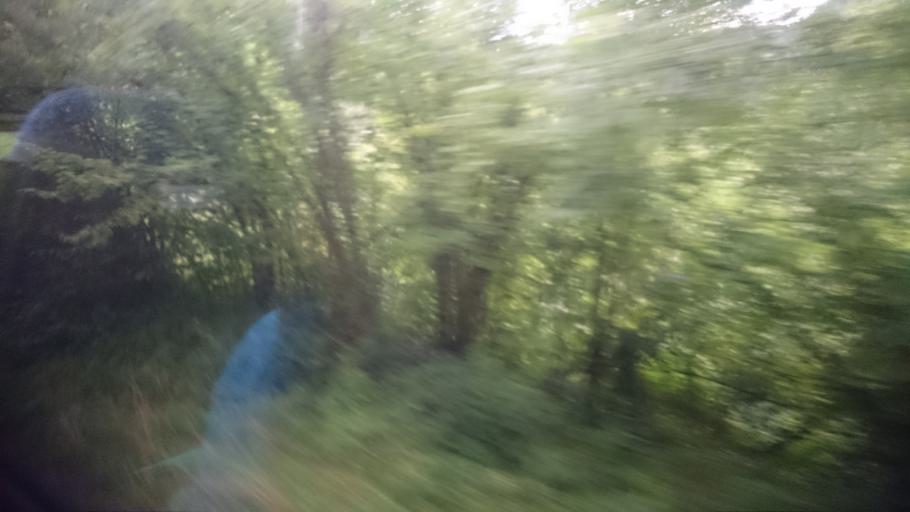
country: ES
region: Asturias
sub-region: Province of Asturias
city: Cangas de Onis
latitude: 43.3180
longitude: -5.0739
